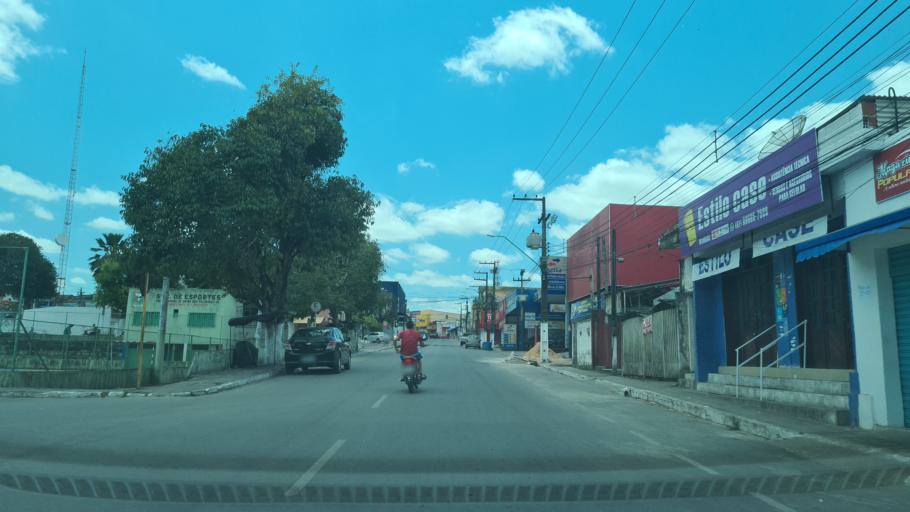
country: BR
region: Alagoas
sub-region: Uniao Dos Palmares
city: Uniao dos Palmares
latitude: -9.1591
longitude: -36.0320
